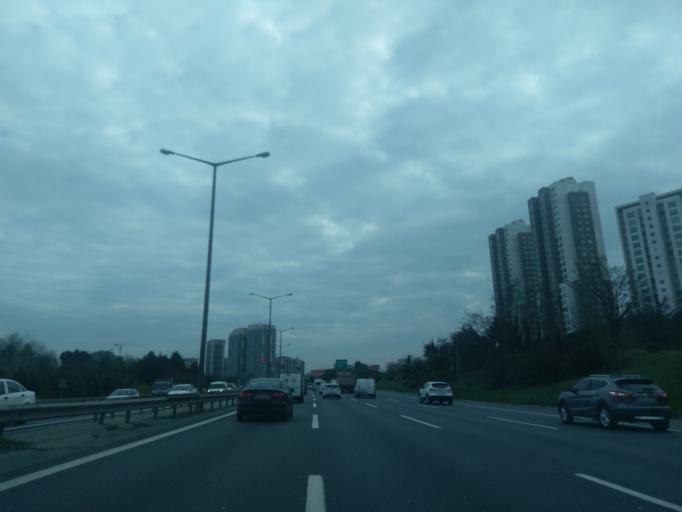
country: TR
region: Istanbul
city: Sisli
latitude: 41.0922
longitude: 28.9365
